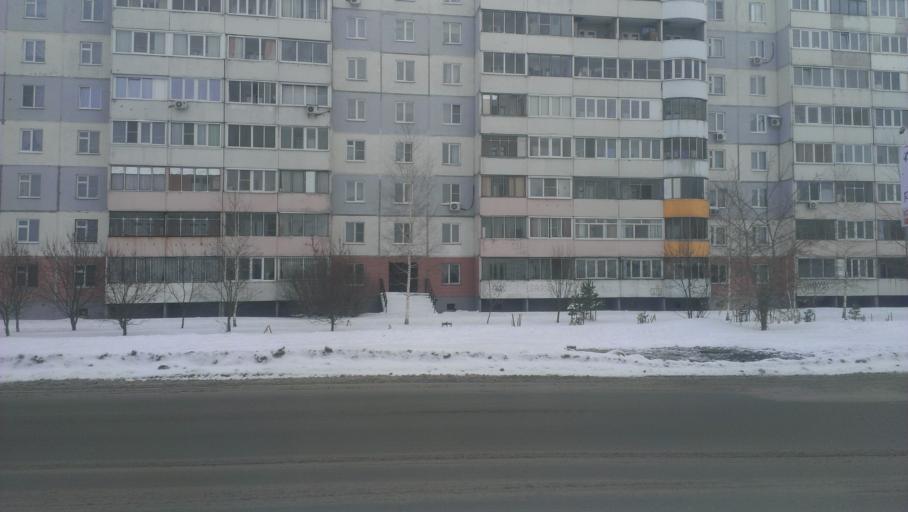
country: RU
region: Altai Krai
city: Novosilikatnyy
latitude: 53.3326
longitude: 83.6685
